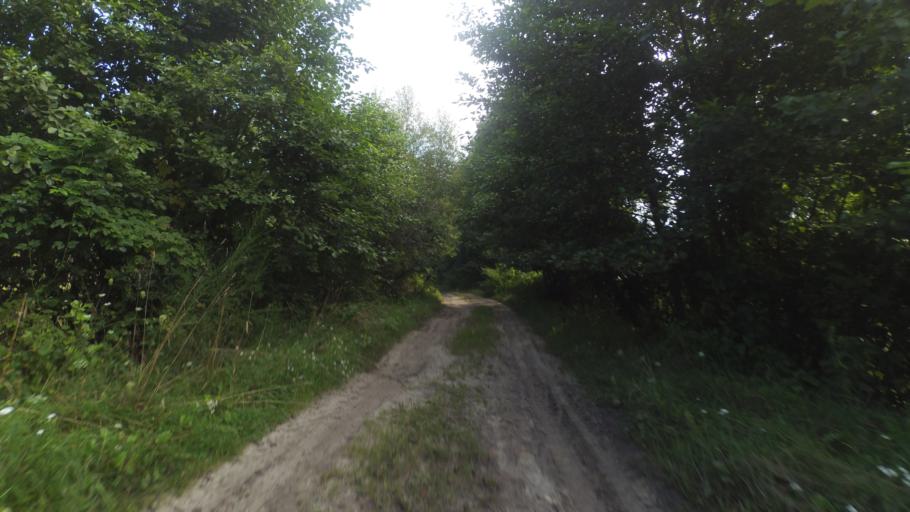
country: PL
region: Lublin Voivodeship
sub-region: Powiat wlodawski
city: Wlodawa
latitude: 51.5011
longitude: 23.6731
